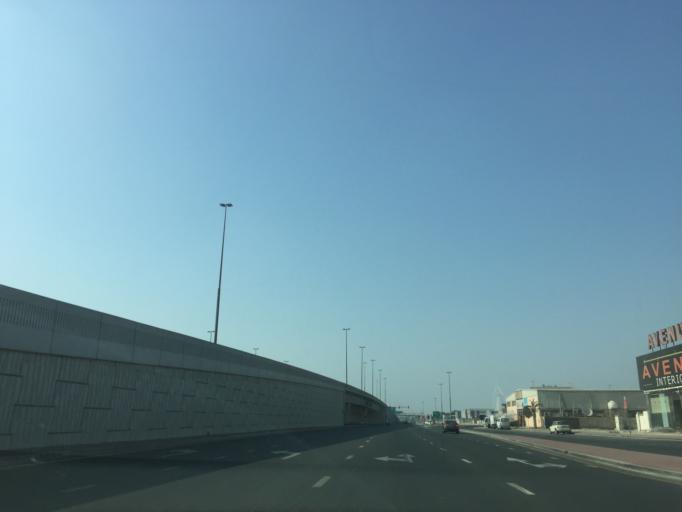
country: AE
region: Dubai
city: Dubai
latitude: 25.1099
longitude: 55.2218
